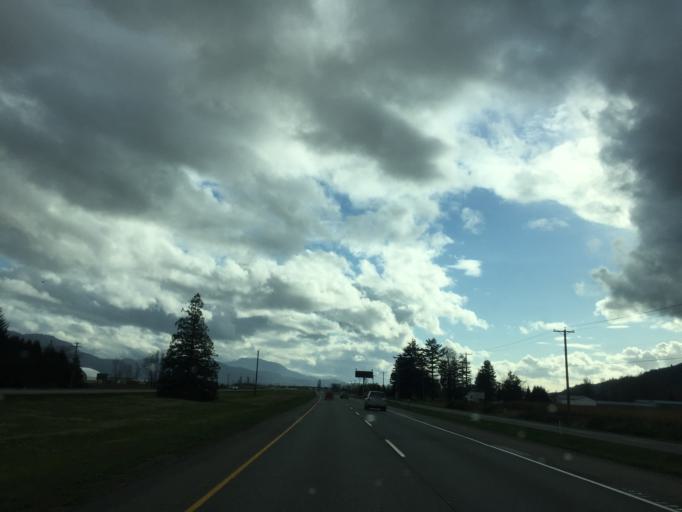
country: CA
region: British Columbia
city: Abbotsford
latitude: 49.1009
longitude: -122.1163
